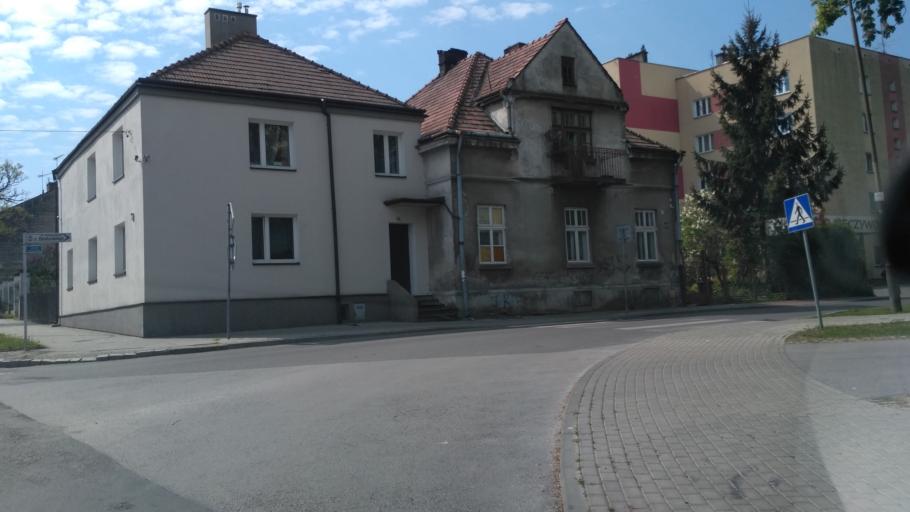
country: PL
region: Subcarpathian Voivodeship
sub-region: Powiat jaroslawski
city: Jaroslaw
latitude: 50.0228
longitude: 22.6748
